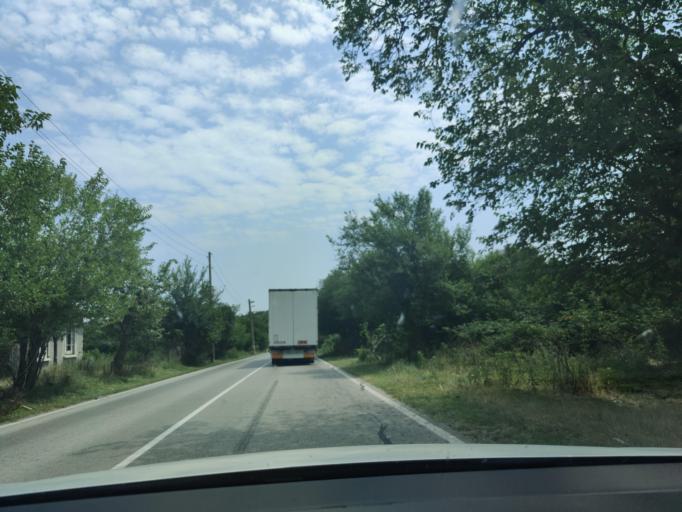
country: BG
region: Vidin
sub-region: Obshtina Ruzhintsi
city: Ruzhintsi
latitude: 43.6554
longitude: 22.7864
